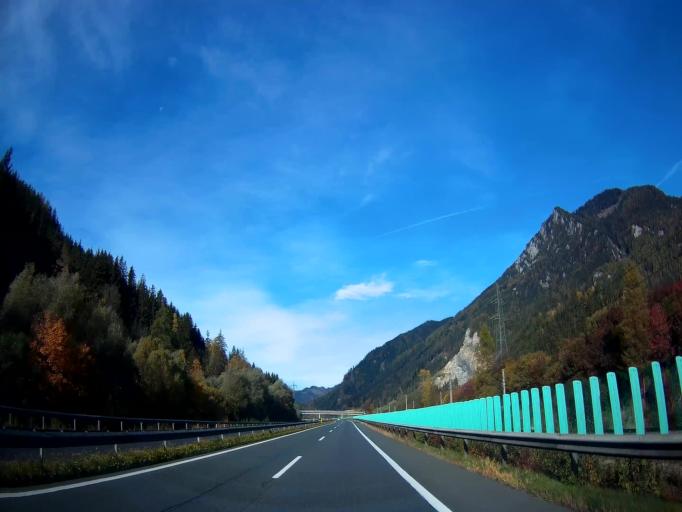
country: AT
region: Styria
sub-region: Politischer Bezirk Leoben
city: Kammern im Liesingtal
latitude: 47.3896
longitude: 14.8832
